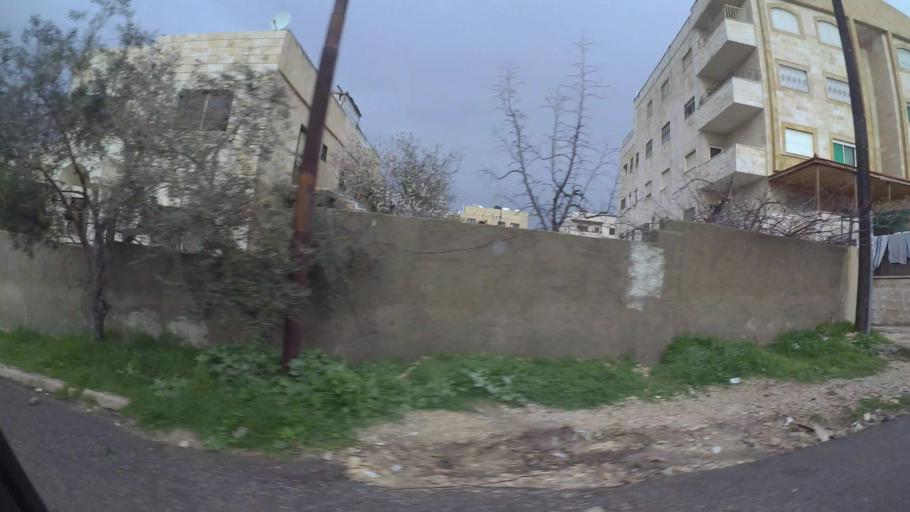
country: JO
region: Amman
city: Al Jubayhah
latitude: 32.0428
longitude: 35.8402
